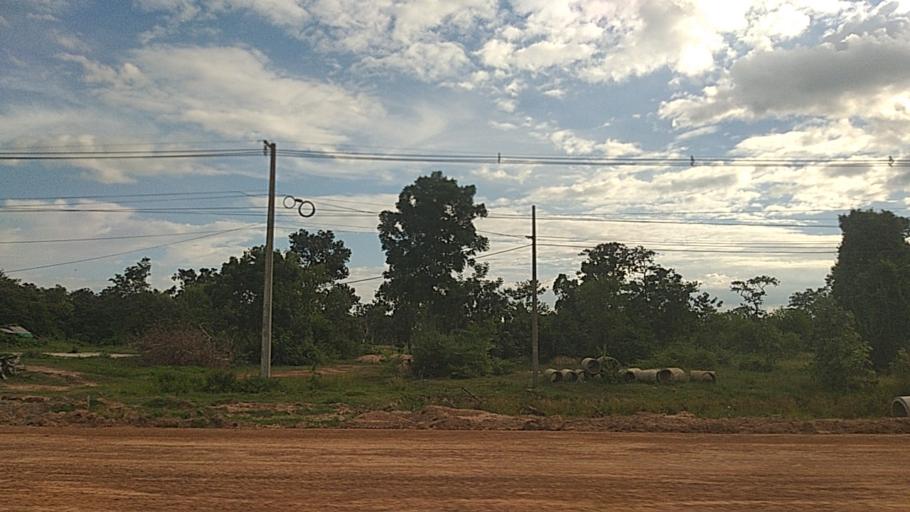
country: TH
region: Surin
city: Kap Choeng
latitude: 14.5147
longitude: 103.5480
